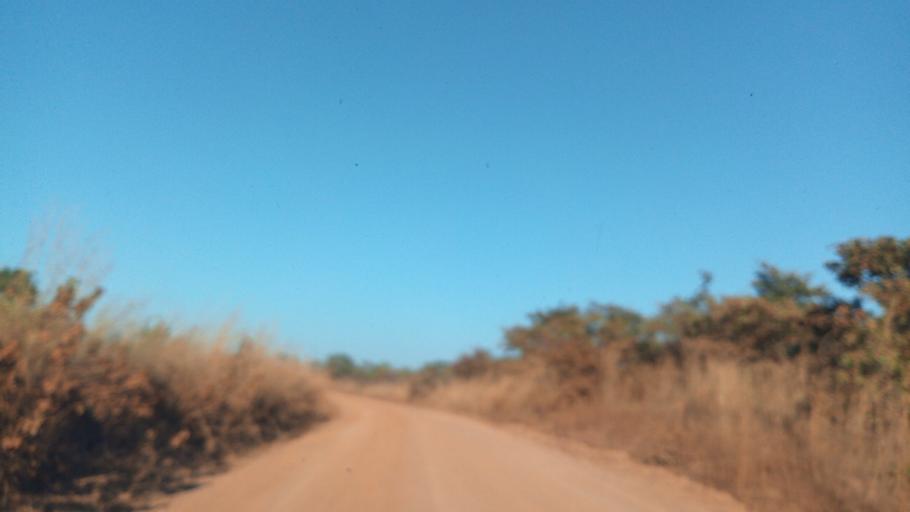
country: ZM
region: Luapula
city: Mwense
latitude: -10.4866
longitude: 28.4890
